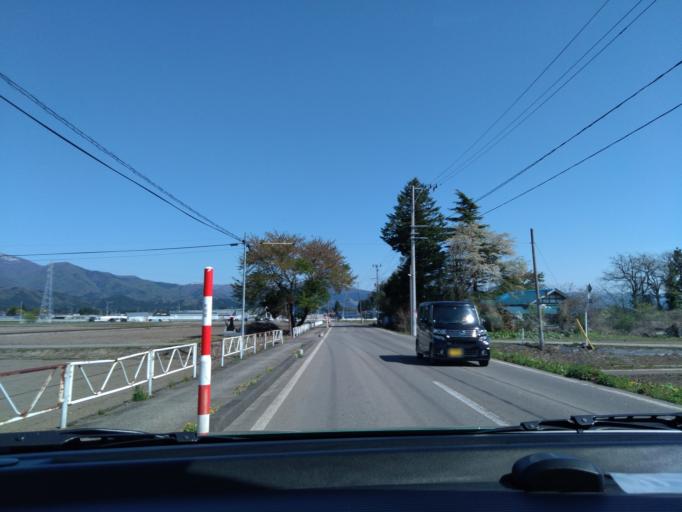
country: JP
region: Akita
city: Kakunodatemachi
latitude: 39.5732
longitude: 140.5761
